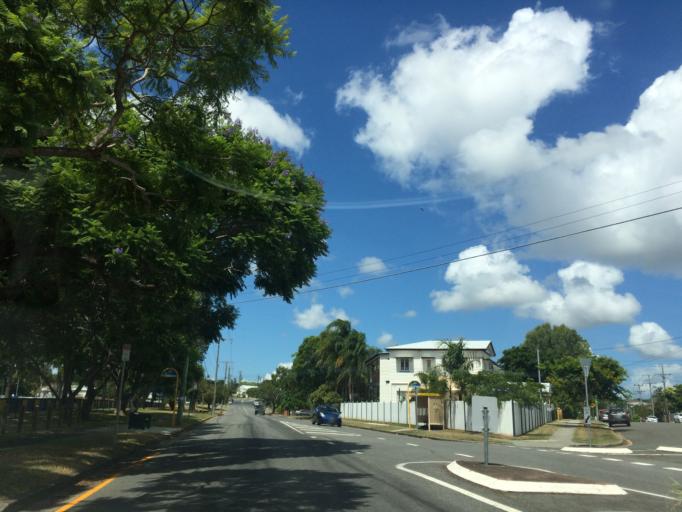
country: AU
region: Queensland
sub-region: Brisbane
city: Seven Hills
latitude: -27.4853
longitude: 153.0603
